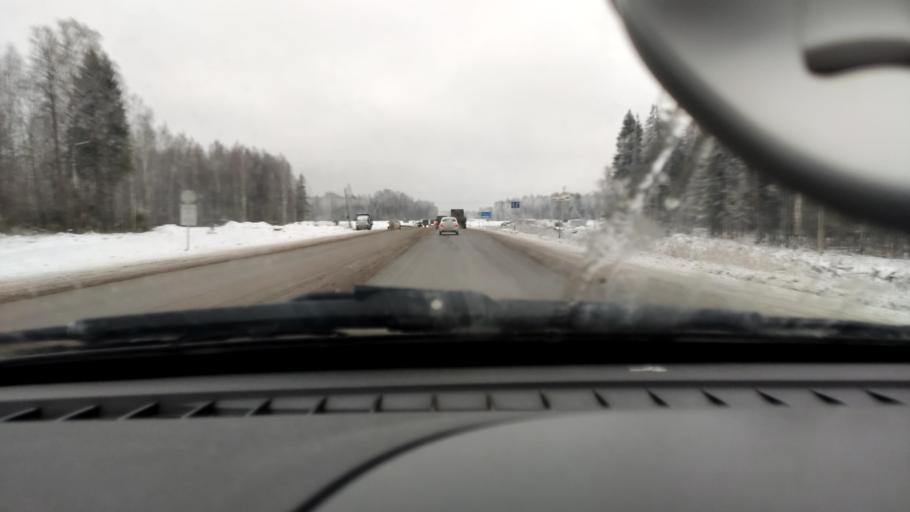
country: RU
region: Perm
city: Polazna
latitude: 58.1409
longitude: 56.4202
